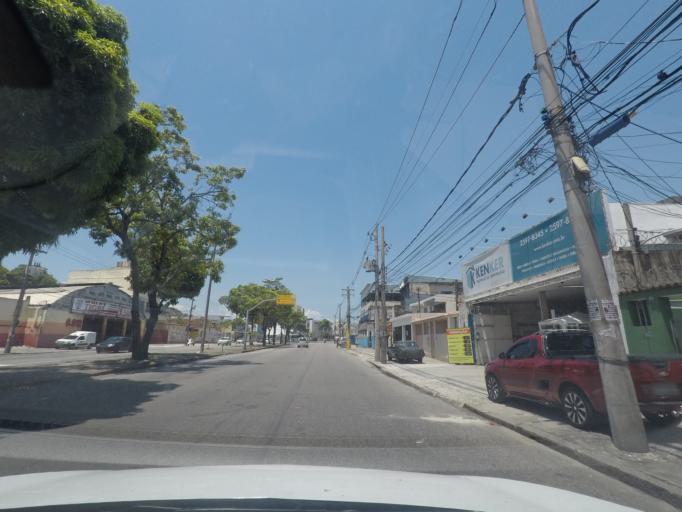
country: BR
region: Rio de Janeiro
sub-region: Rio De Janeiro
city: Rio de Janeiro
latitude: -22.8826
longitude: -43.2956
